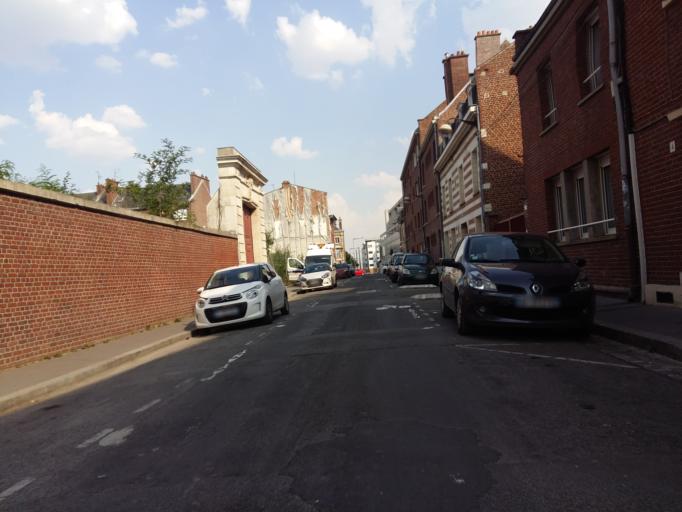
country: FR
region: Picardie
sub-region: Departement de la Somme
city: Amiens
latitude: 49.8928
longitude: 2.3063
